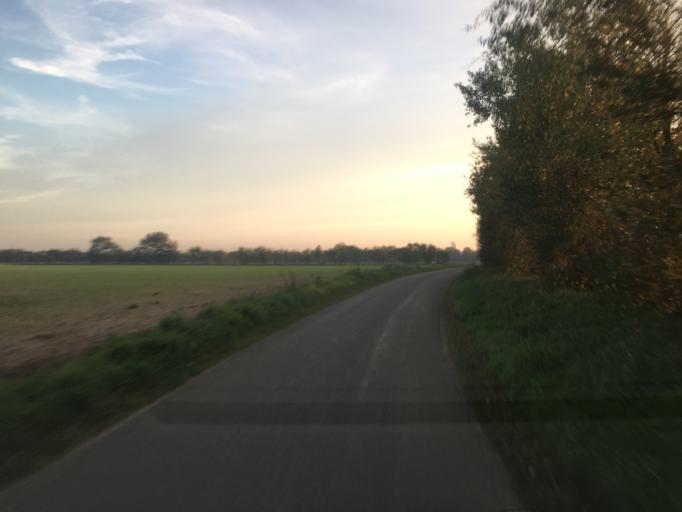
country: DK
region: South Denmark
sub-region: Aabenraa Kommune
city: Tinglev
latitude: 55.0236
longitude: 9.1286
